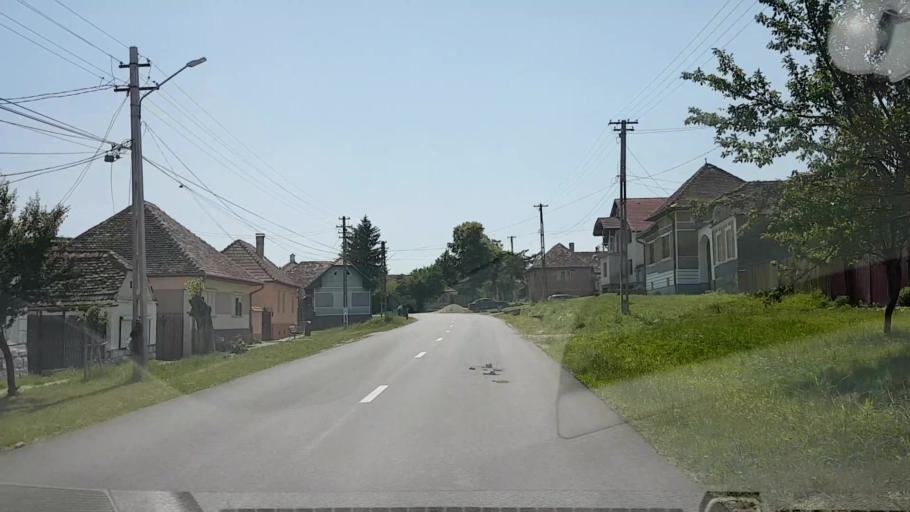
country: RO
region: Sibiu
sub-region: Comuna Merghindeal
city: Merghindeal
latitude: 45.9639
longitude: 24.7335
